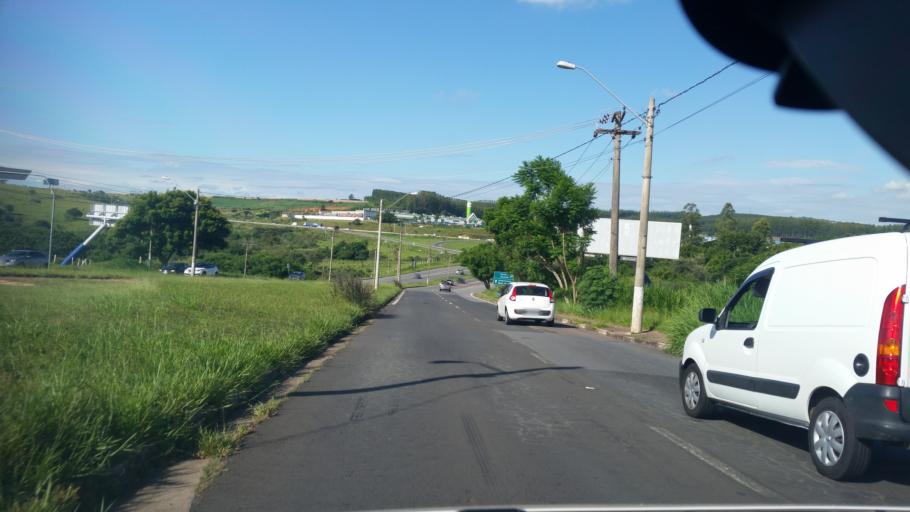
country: BR
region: Sao Paulo
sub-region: Campinas
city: Campinas
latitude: -22.8888
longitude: -47.0173
